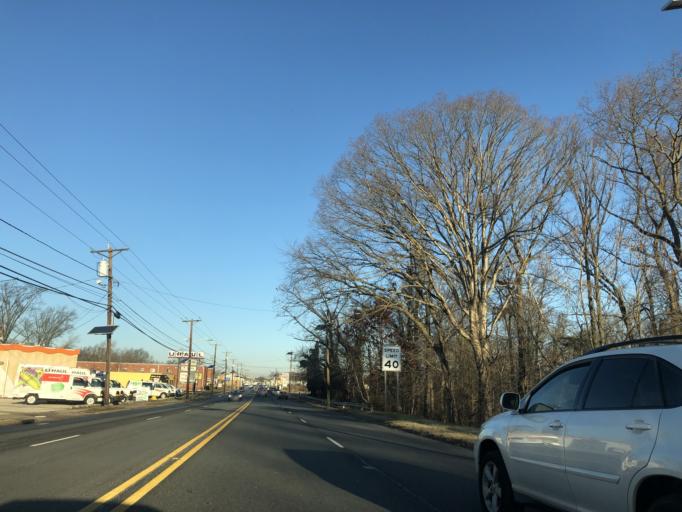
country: US
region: New Jersey
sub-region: Camden County
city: Somerdale
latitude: 39.8487
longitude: -75.0221
